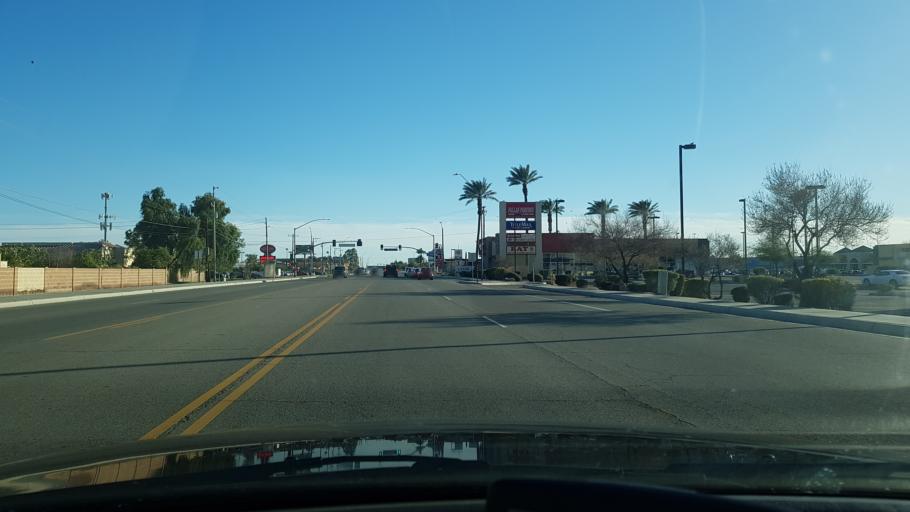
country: US
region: Arizona
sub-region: Yuma County
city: Yuma
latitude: 32.6781
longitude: -114.5989
